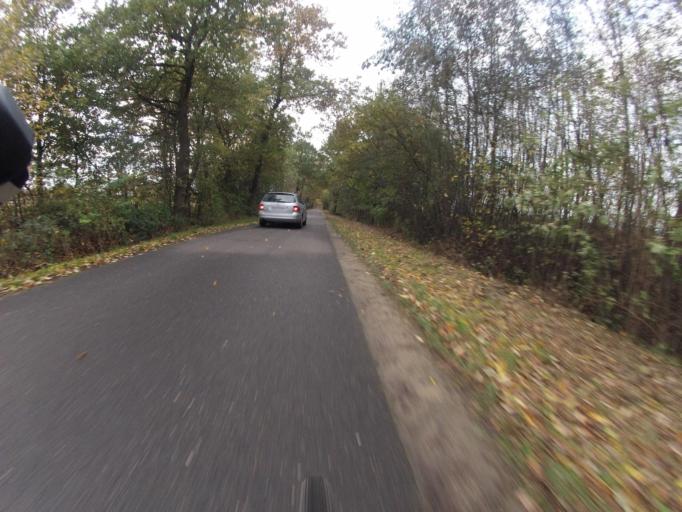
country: DE
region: North Rhine-Westphalia
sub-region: Regierungsbezirk Munster
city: Horstel
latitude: 52.2632
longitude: 7.5618
